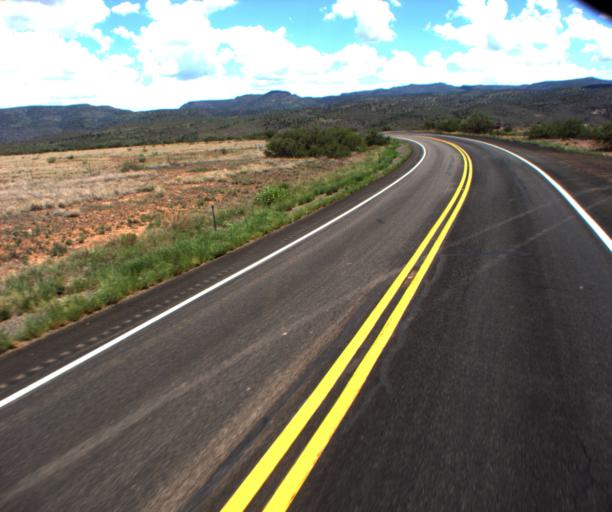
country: US
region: Arizona
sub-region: Yavapai County
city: Camp Verde
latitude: 34.5061
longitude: -111.7627
